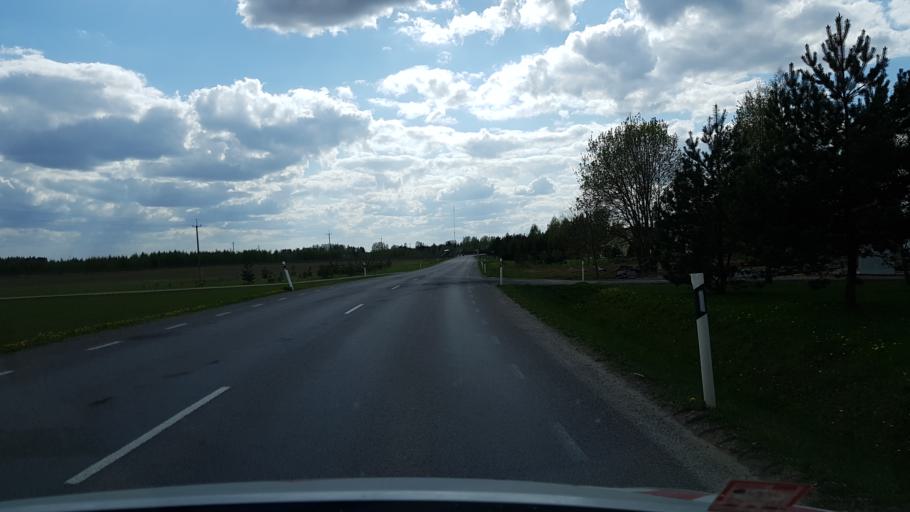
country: EE
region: Tartu
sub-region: Tartu linn
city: Tartu
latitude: 58.3902
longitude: 26.8092
